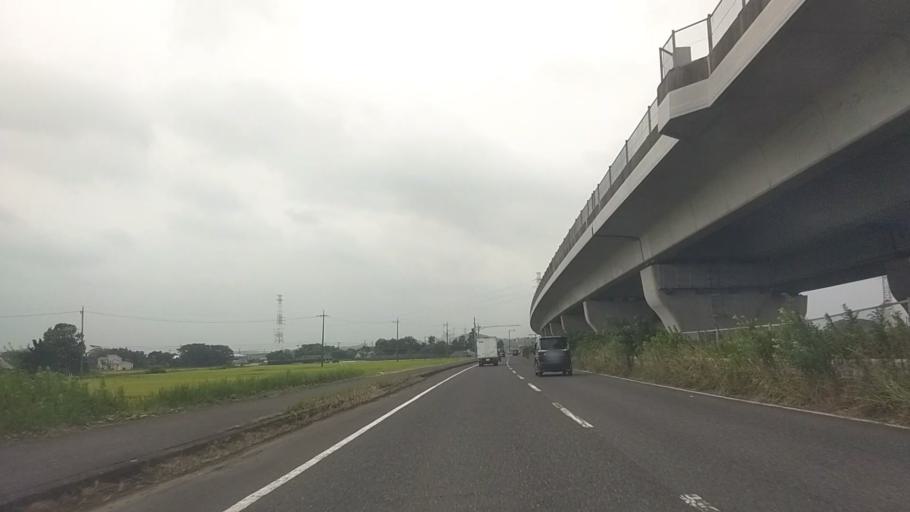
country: JP
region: Chiba
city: Kisarazu
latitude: 35.4050
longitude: 139.9650
